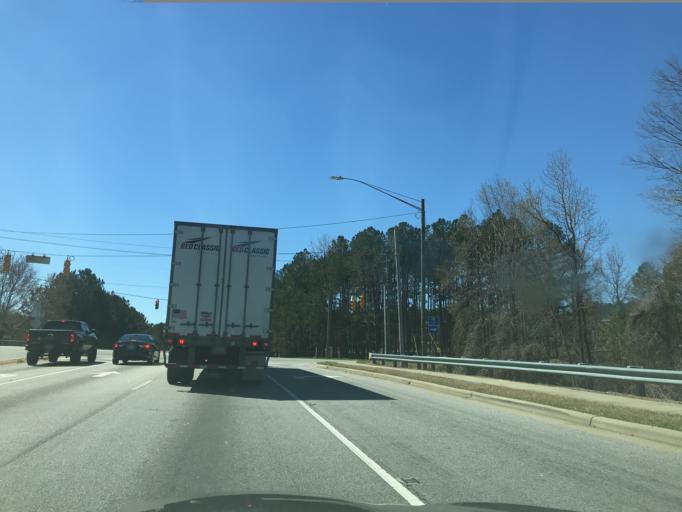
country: US
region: North Carolina
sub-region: Wake County
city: Raleigh
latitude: 35.7431
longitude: -78.6406
